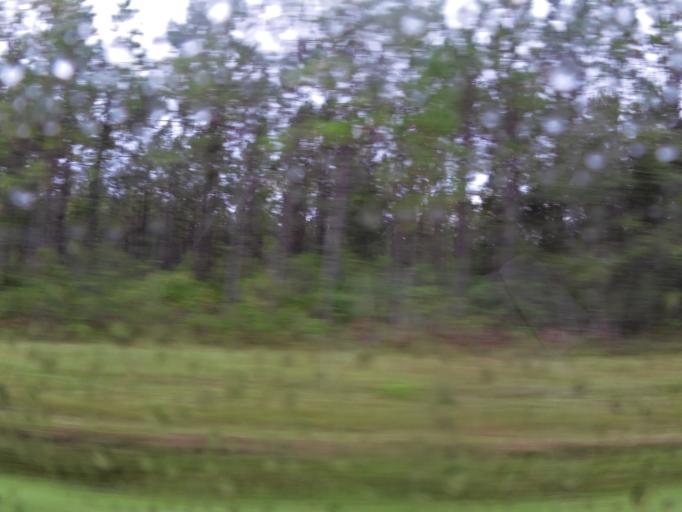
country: US
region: Florida
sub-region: Nassau County
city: Callahan
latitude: 30.5109
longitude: -81.9942
